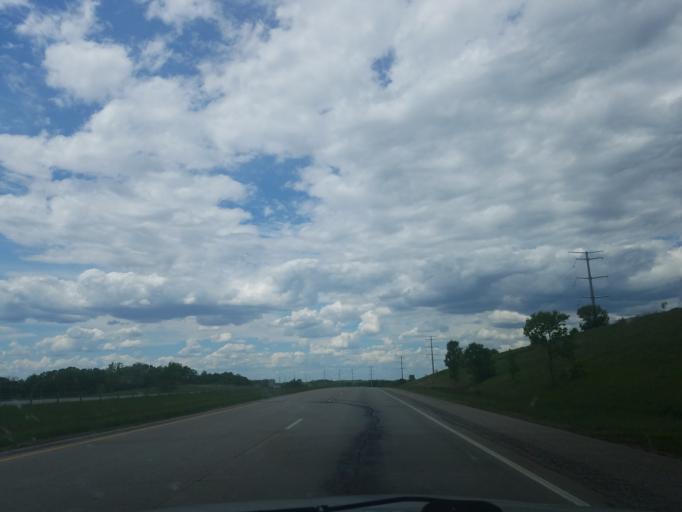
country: US
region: Minnesota
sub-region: Grant County
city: Elbow Lake
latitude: 46.1556
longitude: -95.9513
